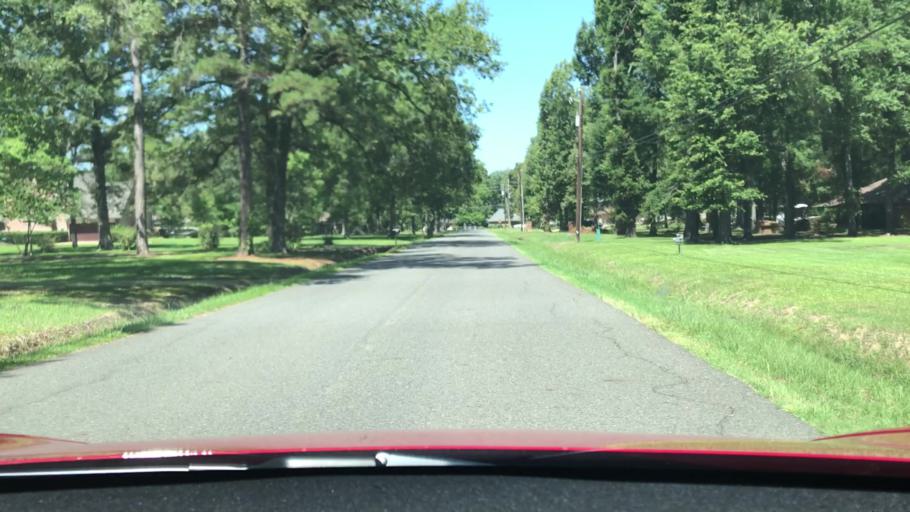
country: US
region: Louisiana
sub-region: De Soto Parish
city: Stonewall
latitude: 32.3449
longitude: -93.7113
